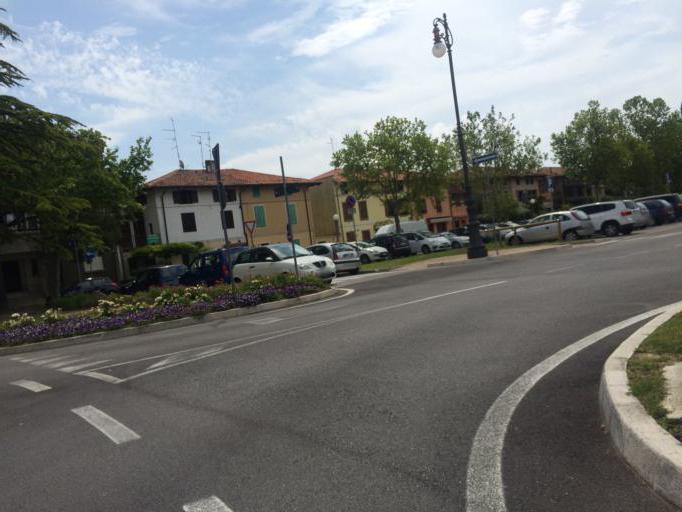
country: IT
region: Friuli Venezia Giulia
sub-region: Provincia di Gorizia
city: Grado
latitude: 45.6811
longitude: 13.3866
